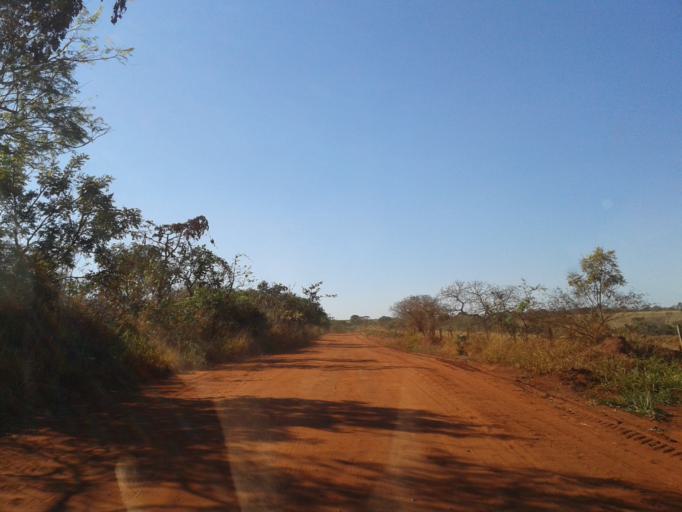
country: BR
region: Minas Gerais
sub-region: Ituiutaba
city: Ituiutaba
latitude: -18.9952
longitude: -49.3751
